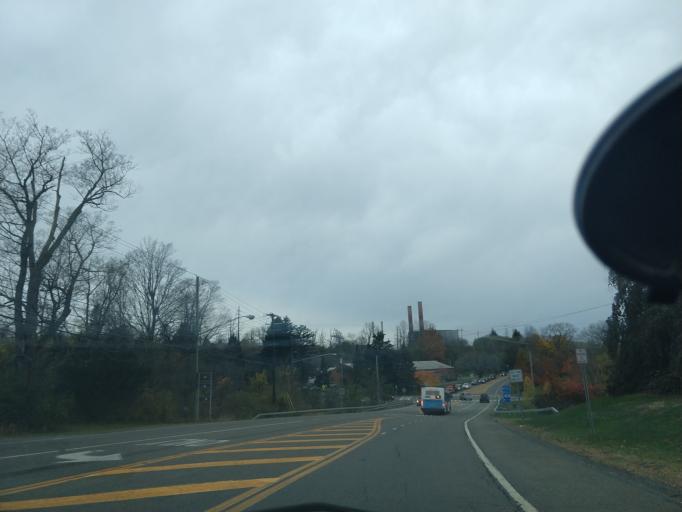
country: US
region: New York
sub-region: Tompkins County
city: East Ithaca
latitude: 42.4439
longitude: -76.4689
